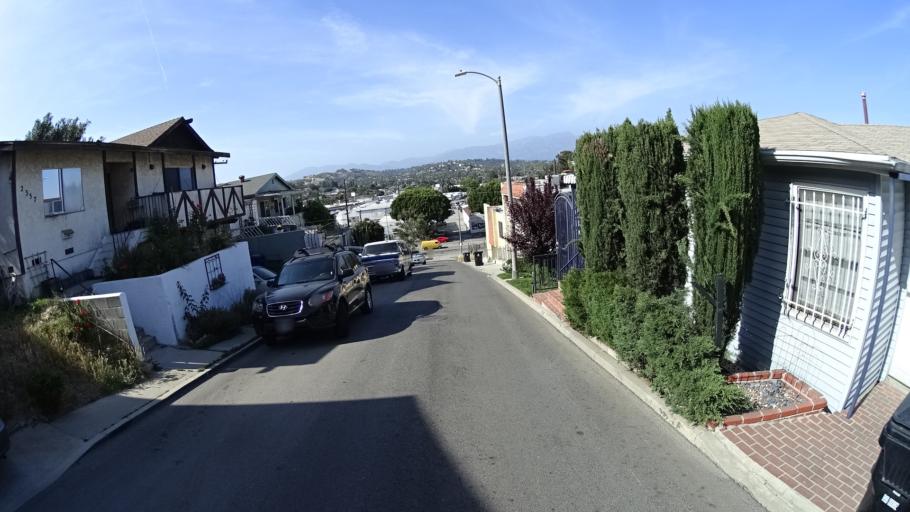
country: US
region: California
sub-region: Los Angeles County
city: Belvedere
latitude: 34.0738
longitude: -118.1672
